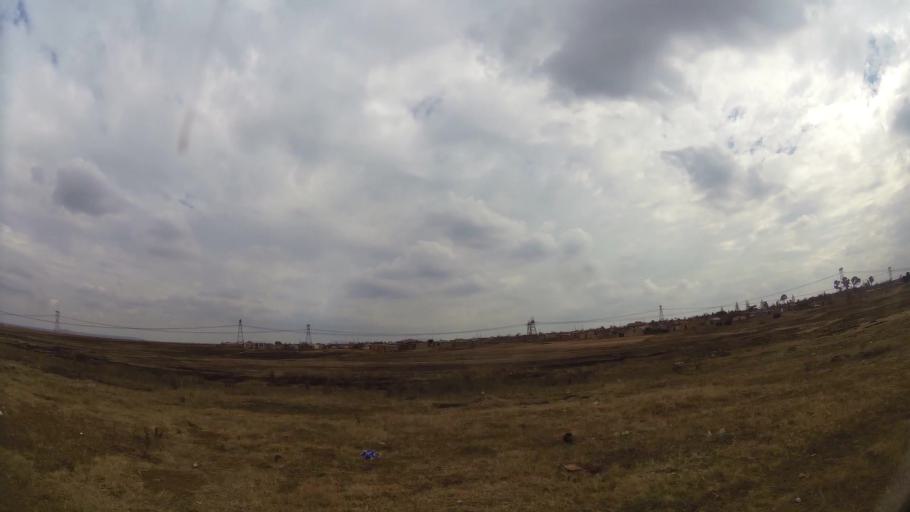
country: ZA
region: Gauteng
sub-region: Ekurhuleni Metropolitan Municipality
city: Germiston
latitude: -26.3803
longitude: 28.1155
